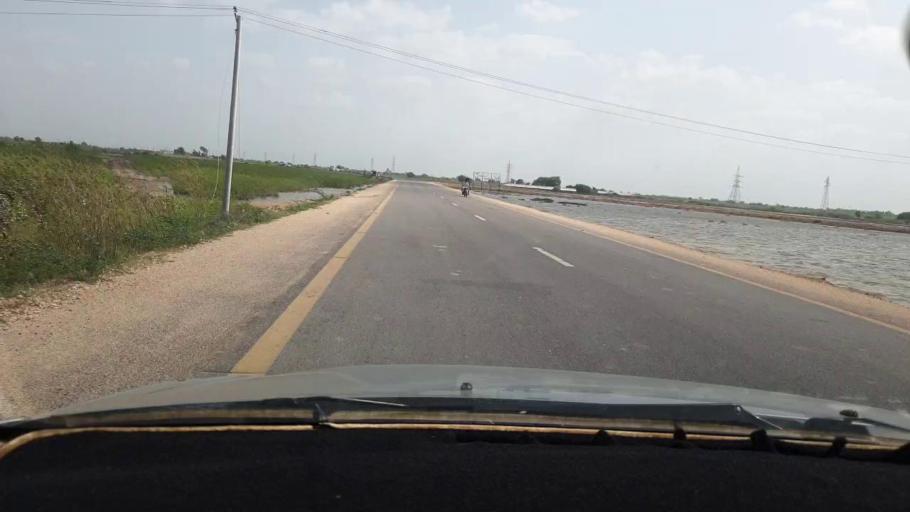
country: PK
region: Sindh
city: Digri
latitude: 25.0545
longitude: 69.2214
